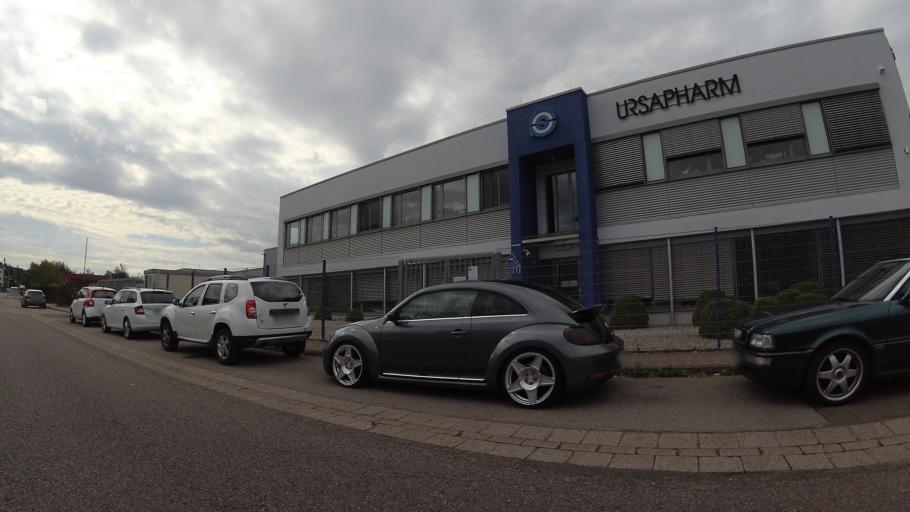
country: DE
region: Saarland
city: Kleinblittersdorf
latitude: 49.1885
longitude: 7.0375
